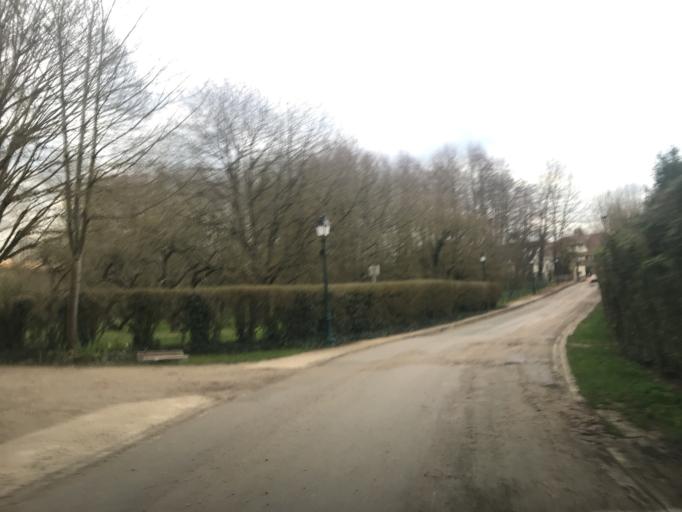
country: FR
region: Ile-de-France
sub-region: Departement des Yvelines
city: Mere
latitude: 48.8148
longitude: 1.8364
